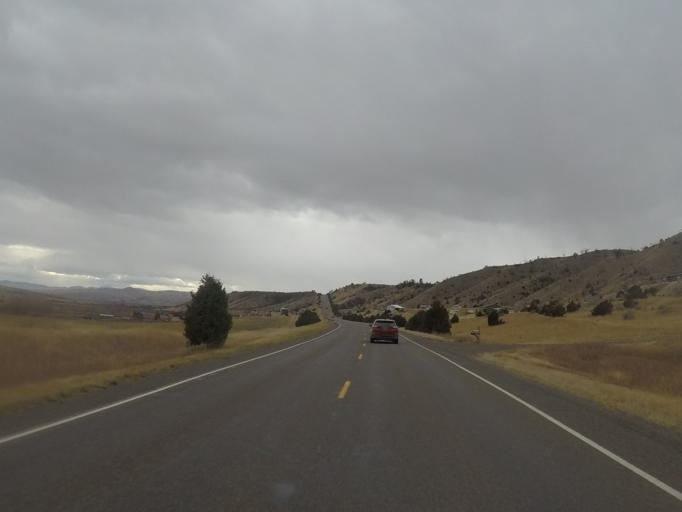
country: US
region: Montana
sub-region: Broadwater County
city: Townsend
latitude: 46.3266
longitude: -111.3978
